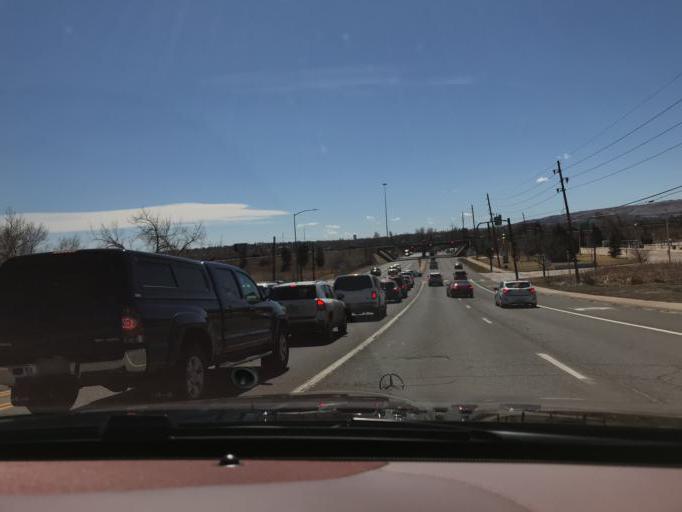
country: US
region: Colorado
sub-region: Jefferson County
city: Applewood
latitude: 39.7824
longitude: -105.1380
